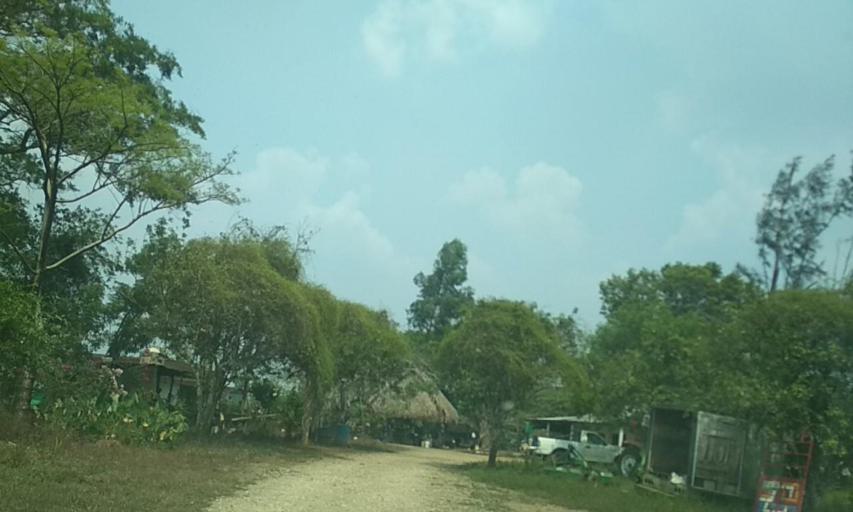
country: MX
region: Tabasco
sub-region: Huimanguillo
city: Francisco Rueda
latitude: 17.8042
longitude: -94.0588
